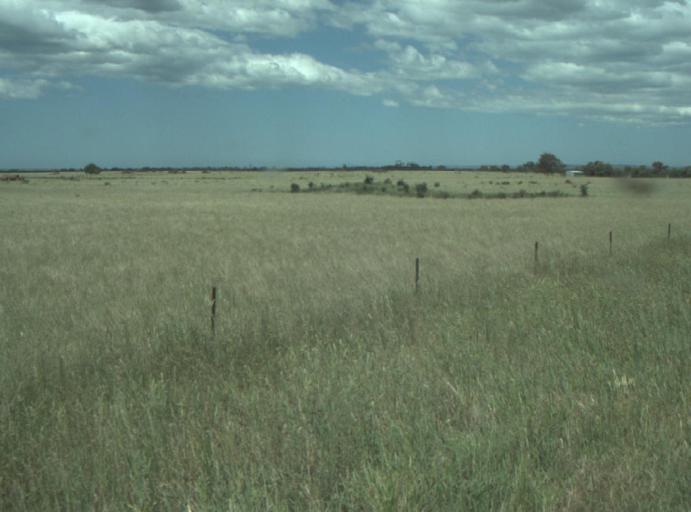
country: AU
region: Victoria
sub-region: Wyndham
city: Little River
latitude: -37.9361
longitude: 144.4658
